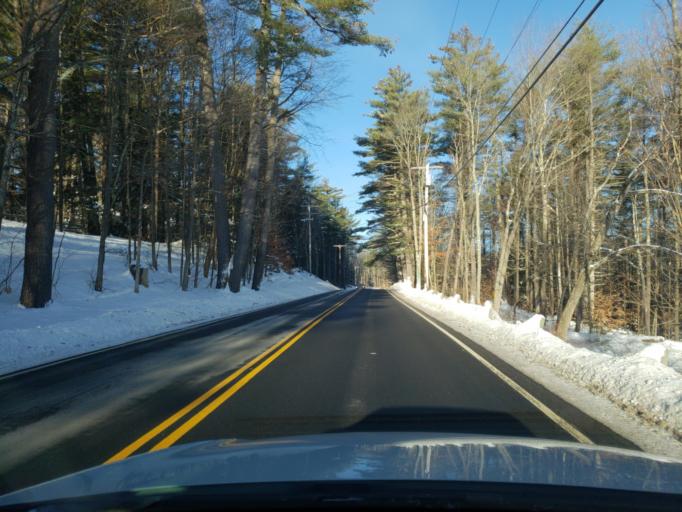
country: US
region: New Hampshire
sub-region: Hillsborough County
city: Greenfield
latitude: 42.9925
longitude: -71.8183
